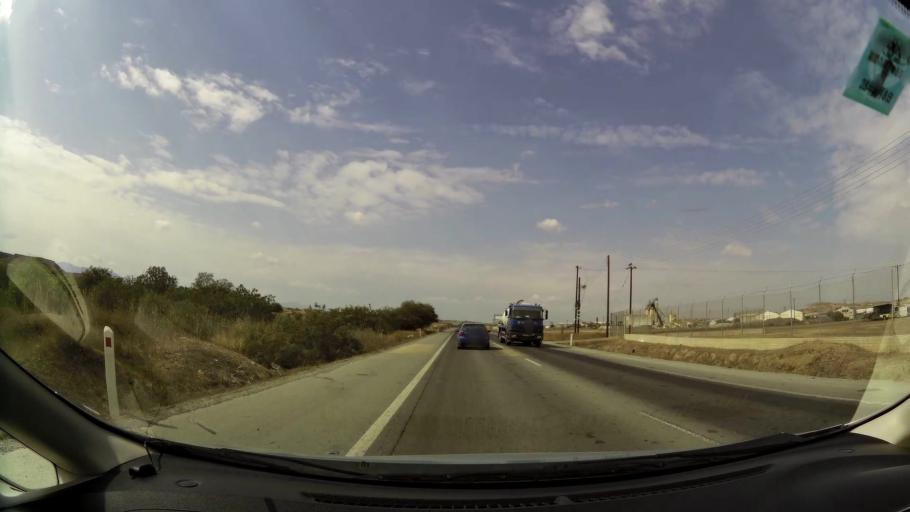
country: CY
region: Lefkosia
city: Tseri
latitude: 35.0593
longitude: 33.3568
